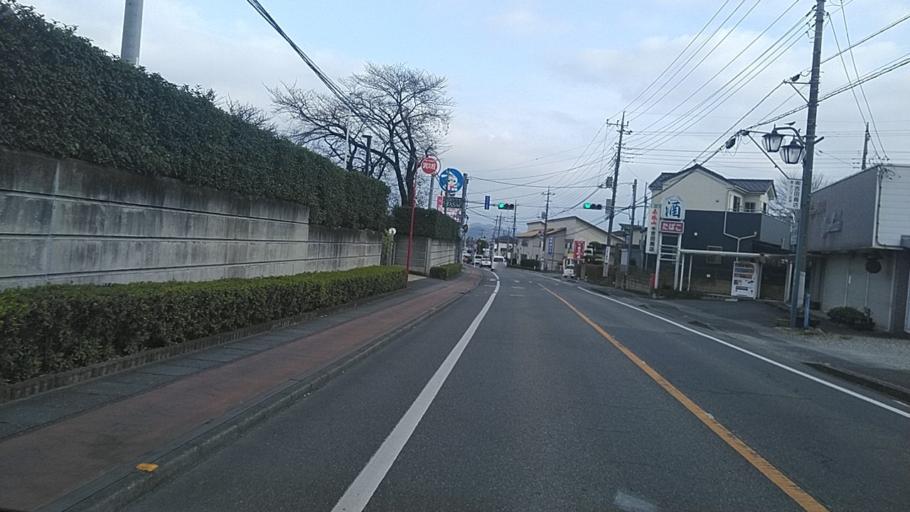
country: JP
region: Gunma
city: Omamacho-omama
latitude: 36.4144
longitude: 139.3009
